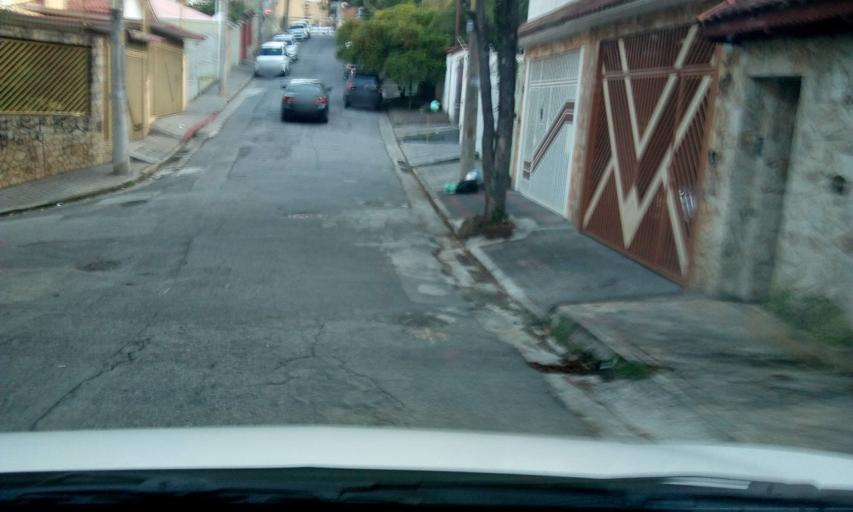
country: BR
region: Sao Paulo
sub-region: Sao Paulo
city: Sao Paulo
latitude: -23.4863
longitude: -46.6138
